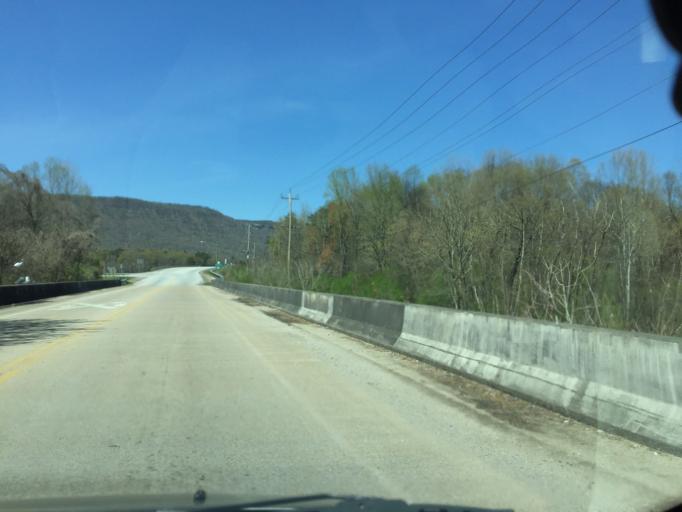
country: US
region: Tennessee
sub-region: Hamilton County
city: Middle Valley
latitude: 35.2110
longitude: -85.2148
